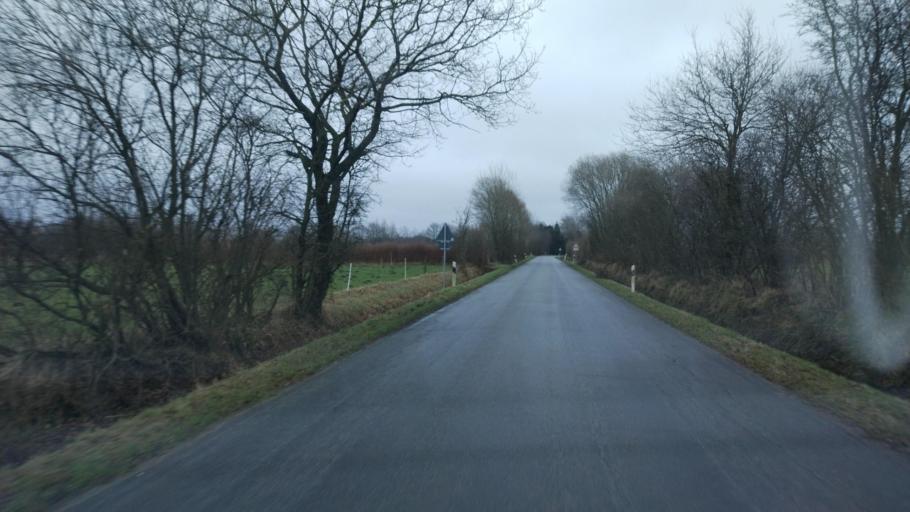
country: DE
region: Schleswig-Holstein
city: Ellingstedt
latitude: 54.4836
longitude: 9.3791
